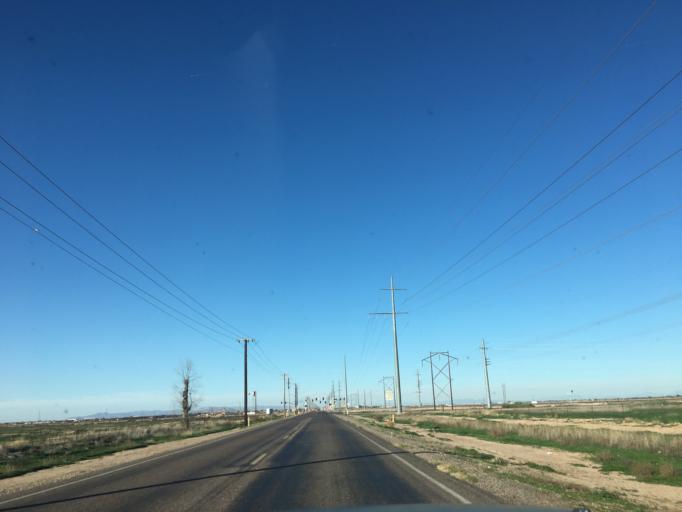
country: US
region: Arizona
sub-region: Pinal County
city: Maricopa
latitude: 33.0218
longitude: -111.9965
